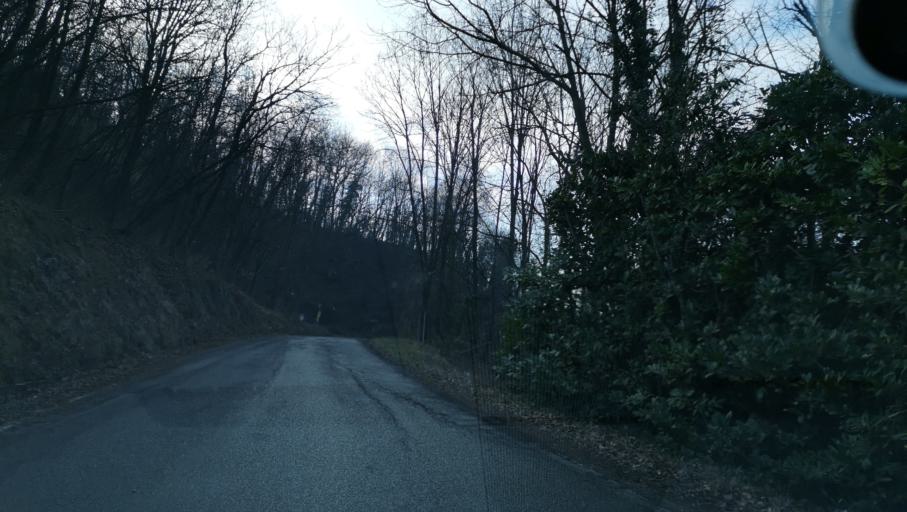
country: IT
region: Piedmont
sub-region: Provincia di Torino
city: Sciolze
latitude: 45.0960
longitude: 7.8873
